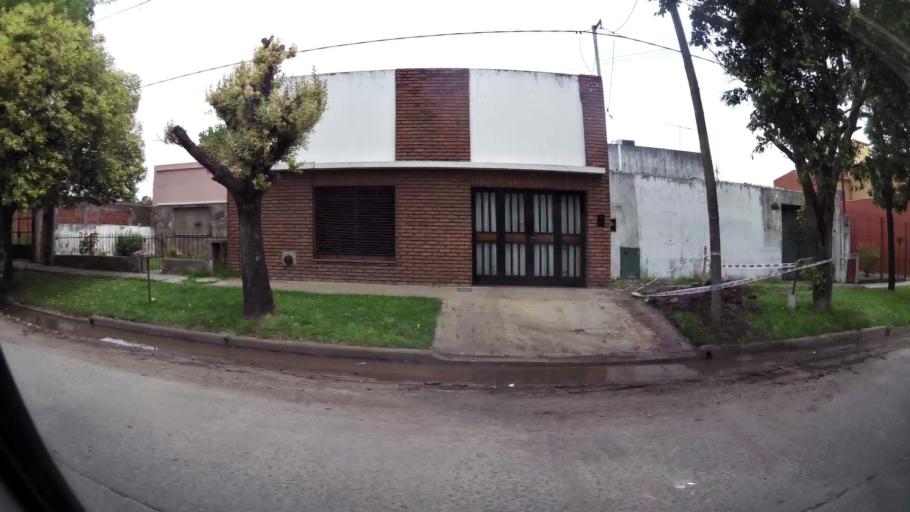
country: AR
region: Buenos Aires
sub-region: Partido de La Plata
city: La Plata
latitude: -34.9467
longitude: -57.9629
